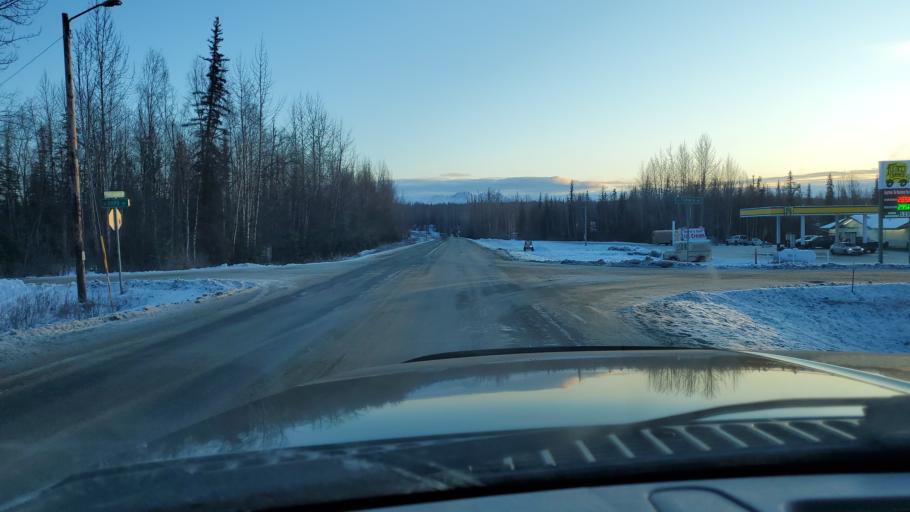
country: US
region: Alaska
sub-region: Matanuska-Susitna Borough
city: Fishhook
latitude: 61.6864
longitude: -149.2405
